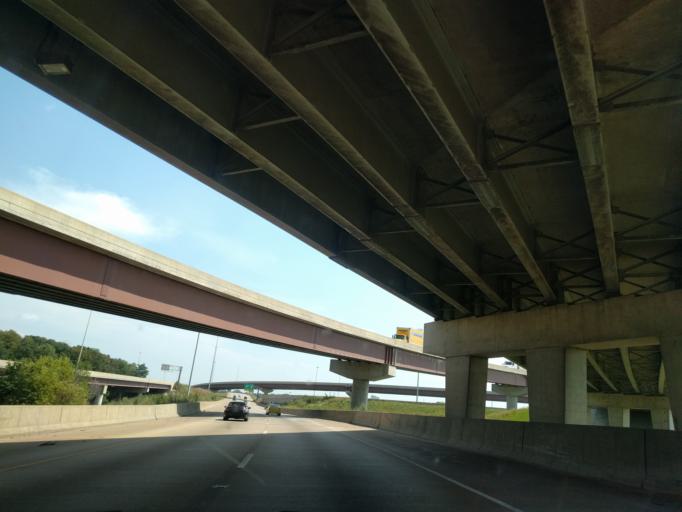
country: US
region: Illinois
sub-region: Cook County
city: Thornton
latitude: 41.5812
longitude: -87.5818
